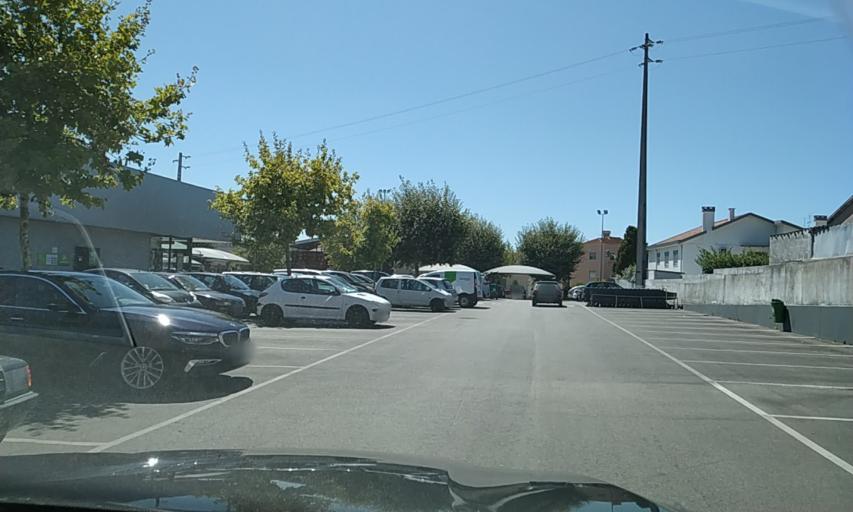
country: PT
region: Leiria
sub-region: Leiria
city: Leiria
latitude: 39.7615
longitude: -8.8207
